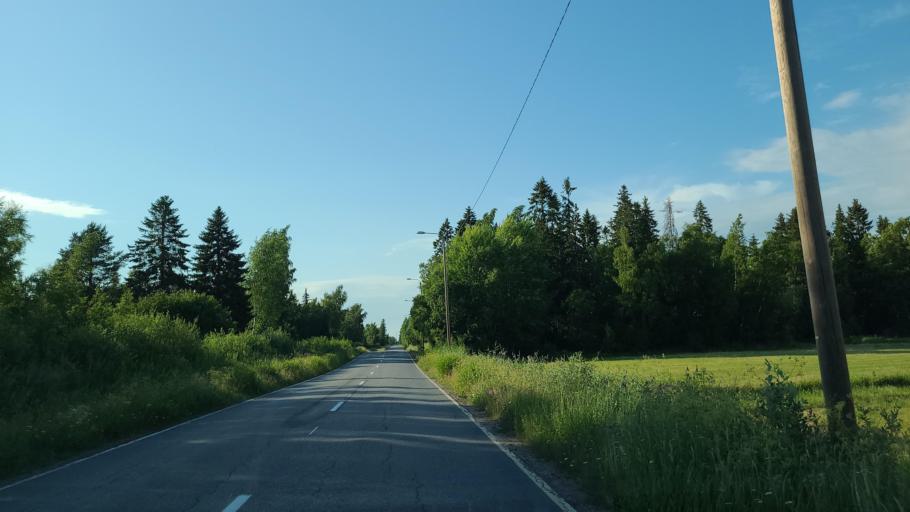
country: FI
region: Ostrobothnia
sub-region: Vaasa
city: Replot
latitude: 63.3258
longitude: 21.3423
